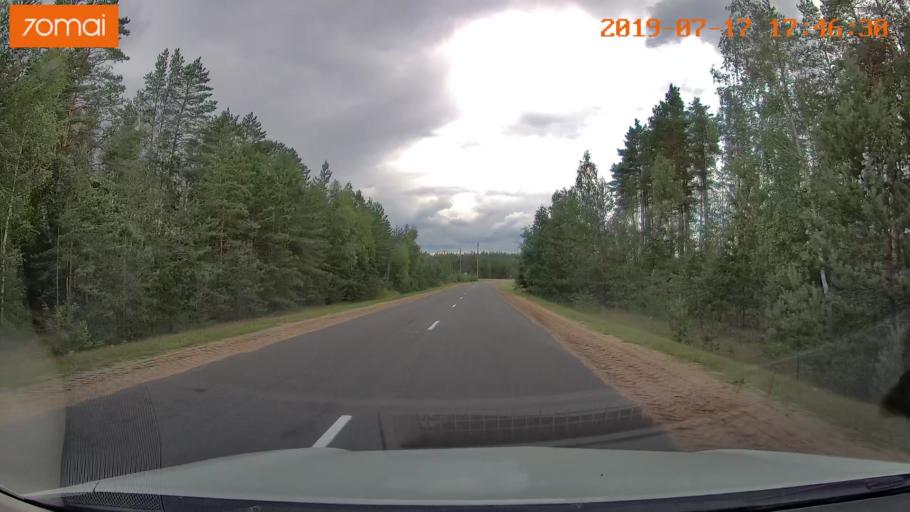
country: BY
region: Mogilev
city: Hlusha
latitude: 53.0990
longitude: 28.8390
